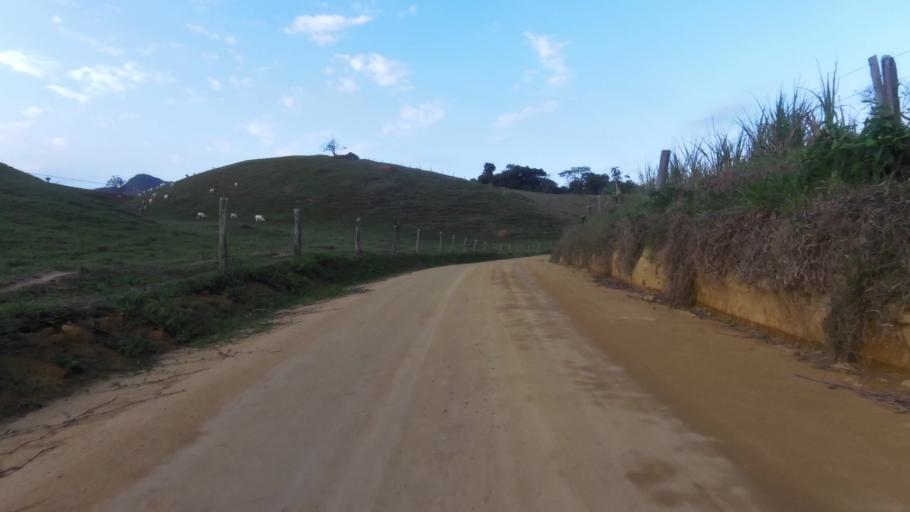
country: BR
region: Espirito Santo
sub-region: Alfredo Chaves
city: Alfredo Chaves
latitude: -20.6997
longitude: -40.6401
